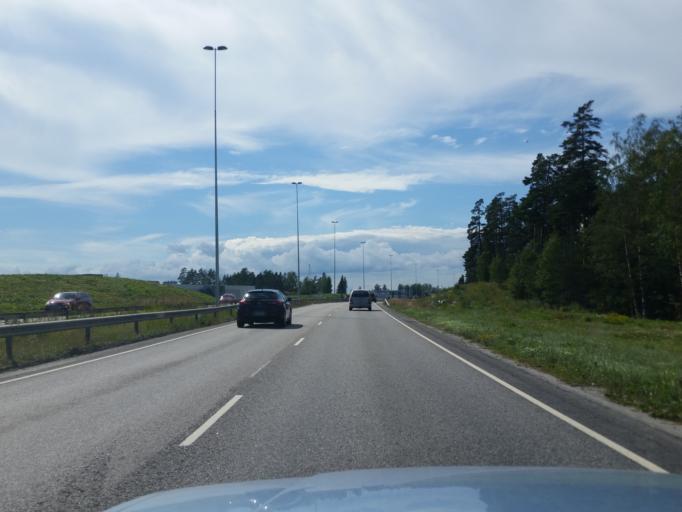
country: FI
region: Uusimaa
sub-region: Helsinki
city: Vantaa
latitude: 60.2972
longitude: 24.9205
